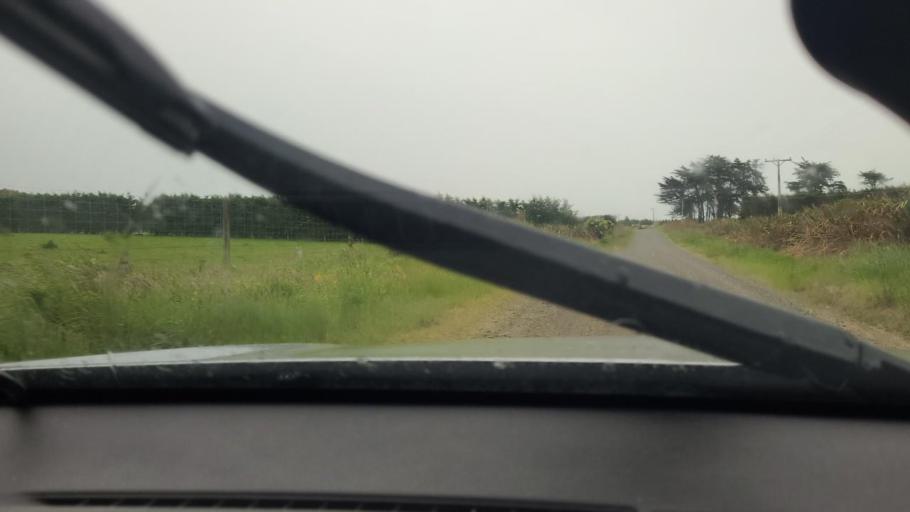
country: NZ
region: Southland
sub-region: Invercargill City
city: Invercargill
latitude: -46.3267
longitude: 168.2369
